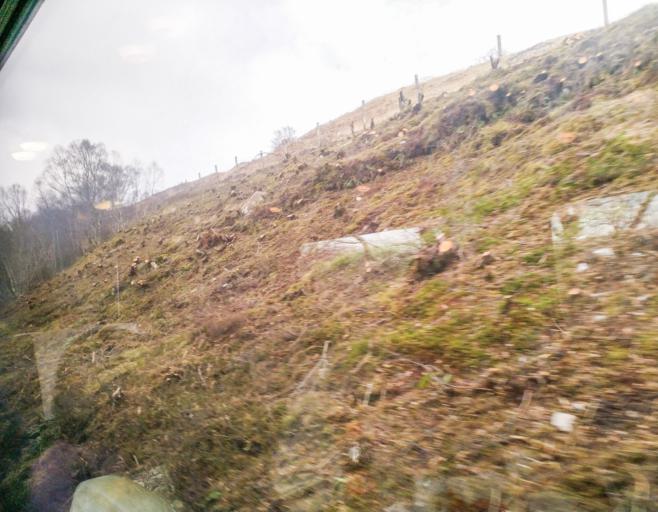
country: GB
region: Scotland
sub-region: Highland
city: Spean Bridge
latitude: 56.7852
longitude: -4.7318
